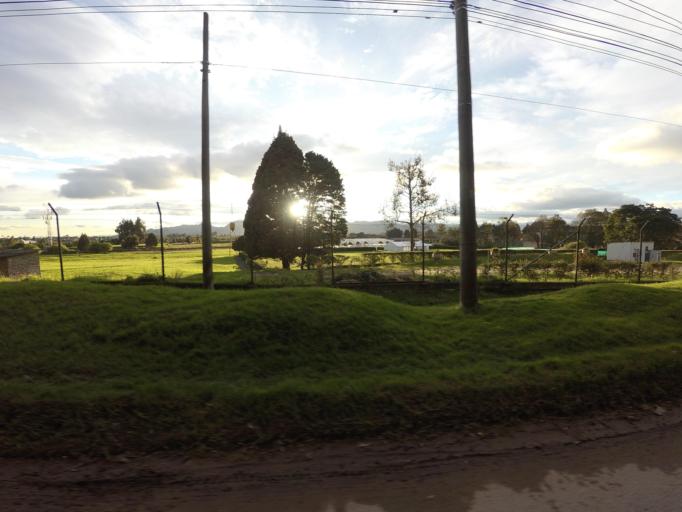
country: CO
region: Cundinamarca
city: Chia
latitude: 4.7971
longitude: -74.0313
